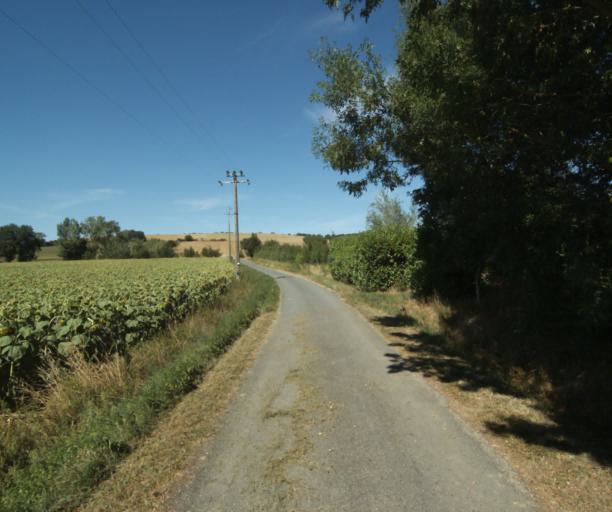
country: FR
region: Midi-Pyrenees
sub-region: Departement de la Haute-Garonne
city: Saint-Felix-Lauragais
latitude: 43.5170
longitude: 1.8957
